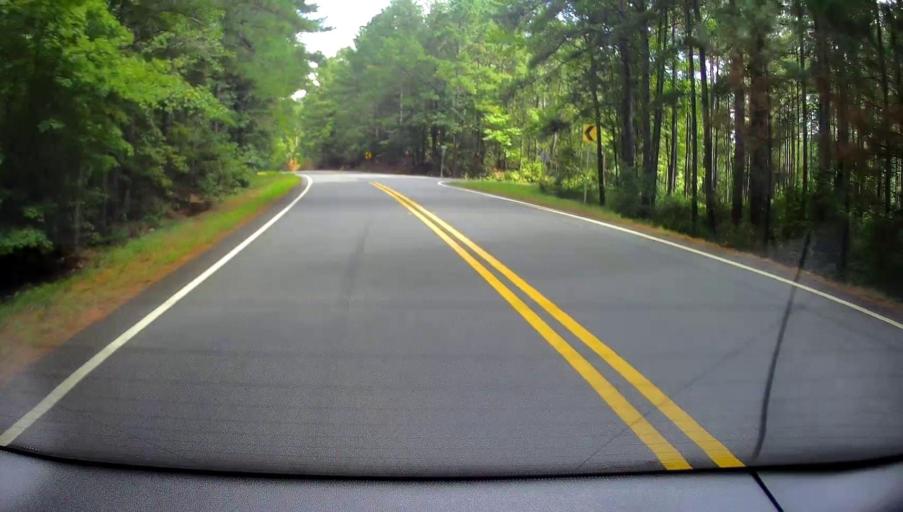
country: US
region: Georgia
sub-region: Monroe County
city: Forsyth
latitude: 32.8795
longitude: -83.9599
